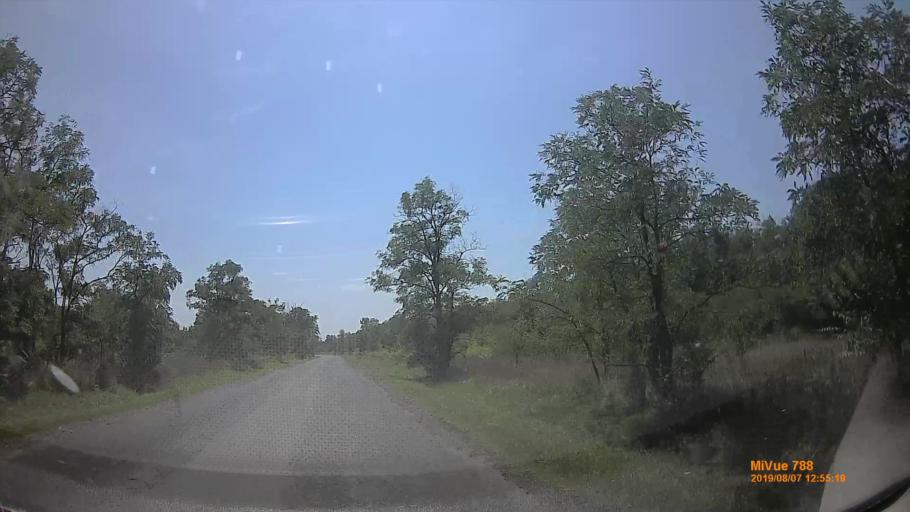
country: HU
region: Zala
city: Gyenesdias
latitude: 46.8121
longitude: 17.2702
